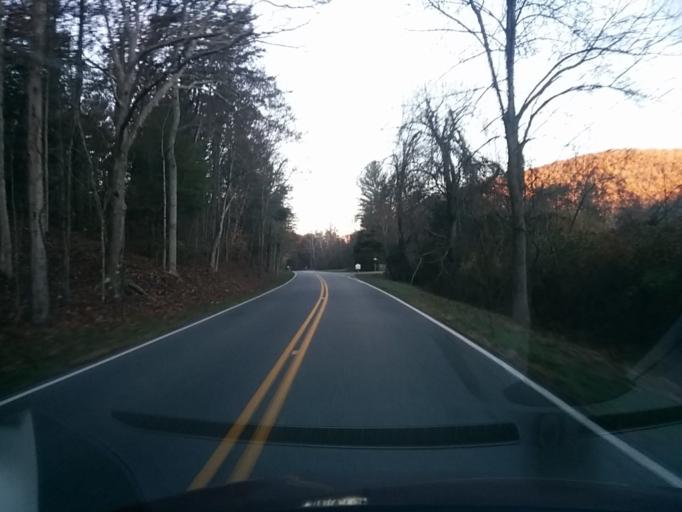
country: US
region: Virginia
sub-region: Rockbridge County
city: East Lexington
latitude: 37.9581
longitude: -79.4731
